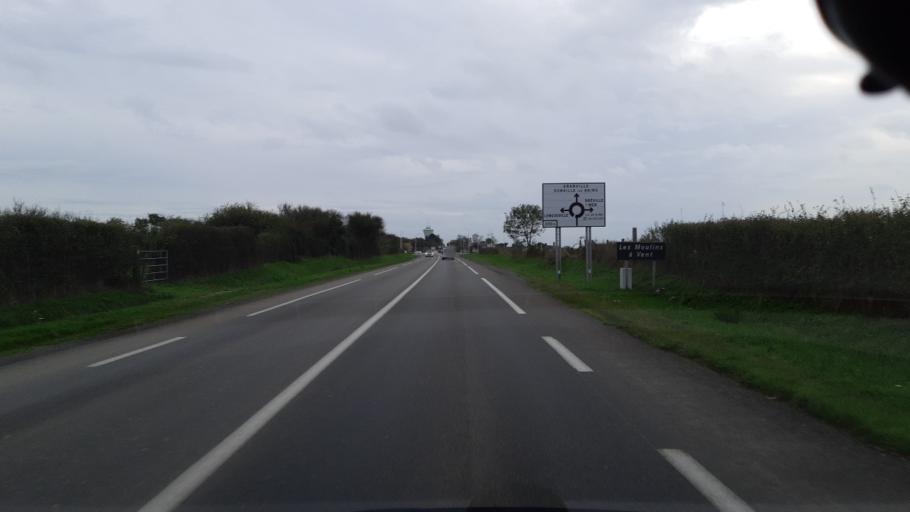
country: FR
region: Lower Normandy
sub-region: Departement de la Manche
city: Donville-les-Bains
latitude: 48.8603
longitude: -1.5520
